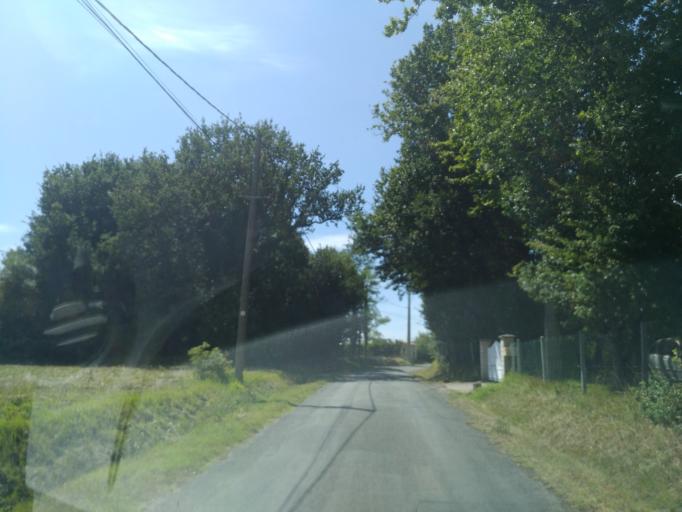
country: FR
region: Poitou-Charentes
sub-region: Departement de la Charente-Maritime
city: Breuillet
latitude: 45.7005
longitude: -1.0663
